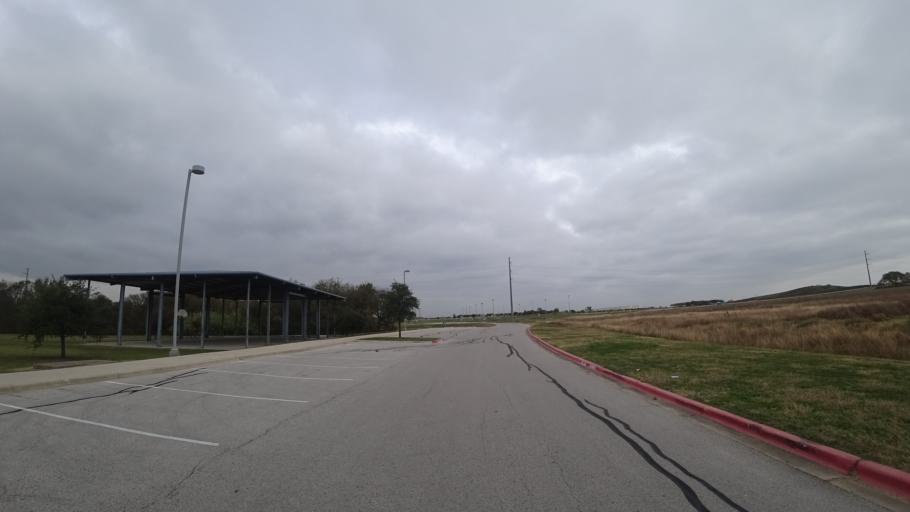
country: US
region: Texas
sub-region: Travis County
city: Pflugerville
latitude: 30.4074
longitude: -97.5974
